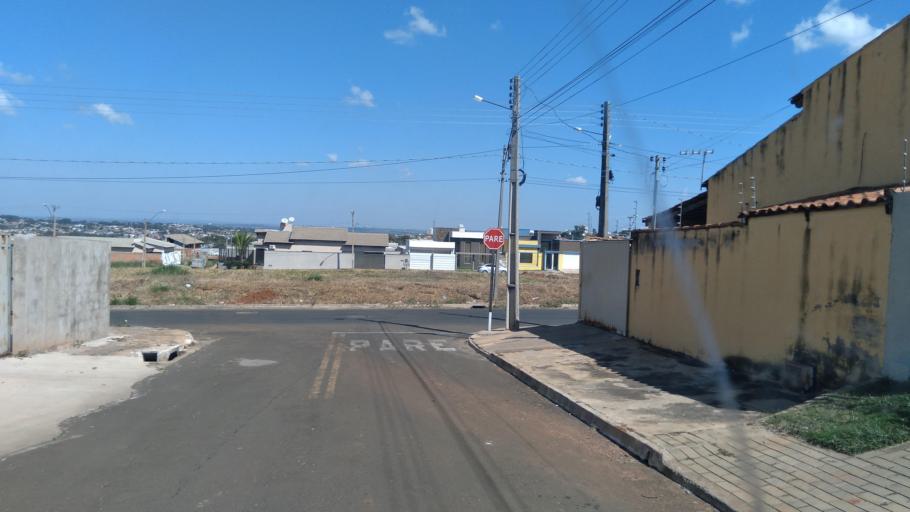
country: BR
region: Goias
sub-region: Mineiros
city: Mineiros
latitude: -17.5497
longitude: -52.5418
